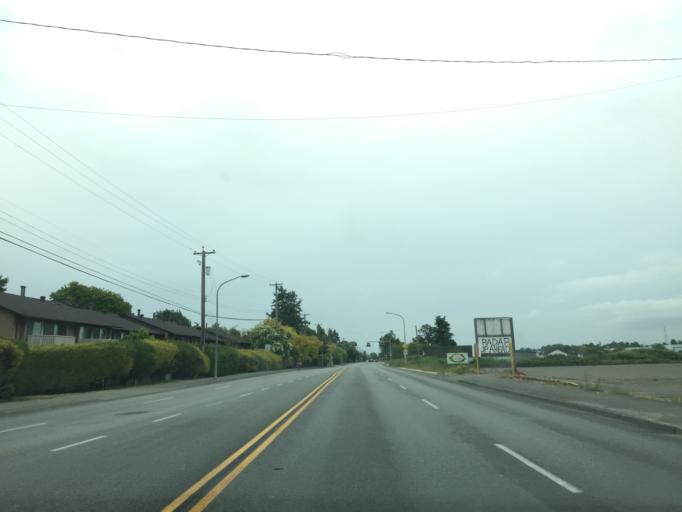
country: CA
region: British Columbia
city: Richmond
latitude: 49.1334
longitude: -123.1136
